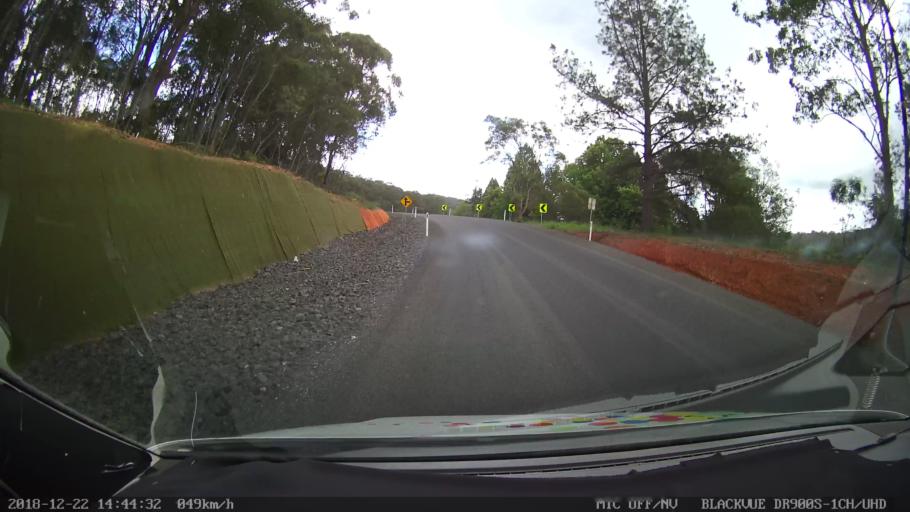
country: AU
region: New South Wales
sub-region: Bellingen
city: Dorrigo
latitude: -30.1658
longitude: 152.5760
